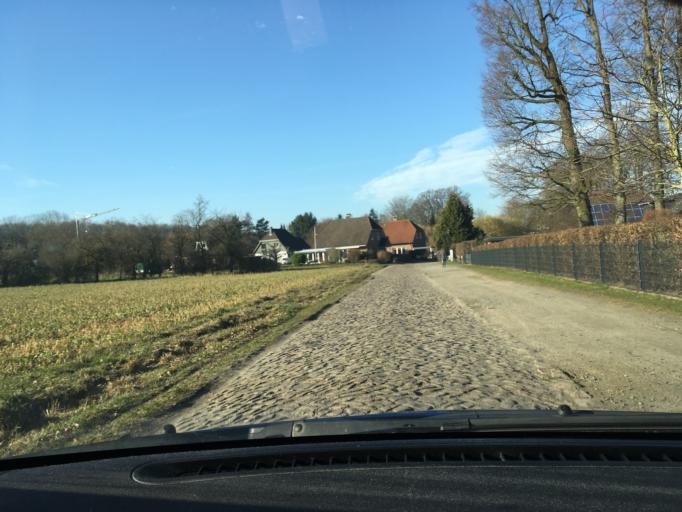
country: DE
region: Lower Saxony
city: Seevetal
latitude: 53.4046
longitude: 9.9896
